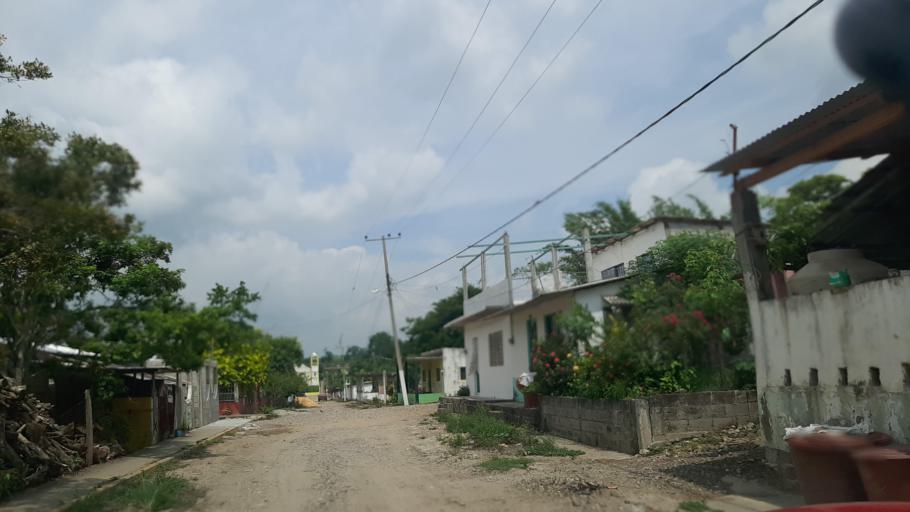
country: MX
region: Veracruz
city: Gutierrez Zamora
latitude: 20.4466
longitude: -97.1626
